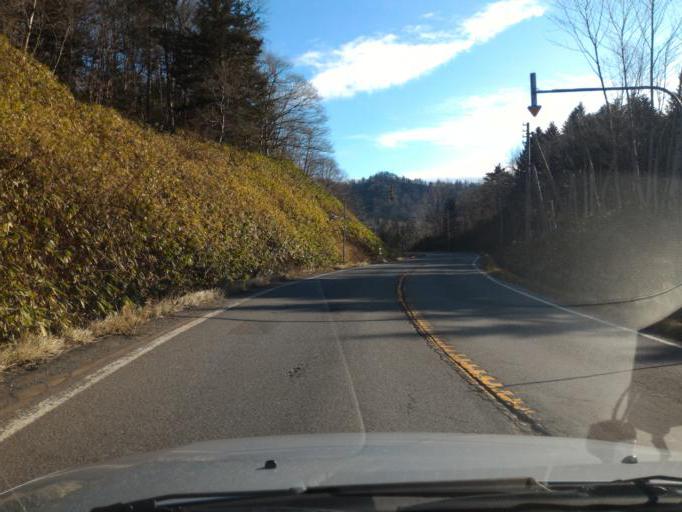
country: JP
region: Hokkaido
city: Bibai
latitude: 43.2814
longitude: 142.0603
